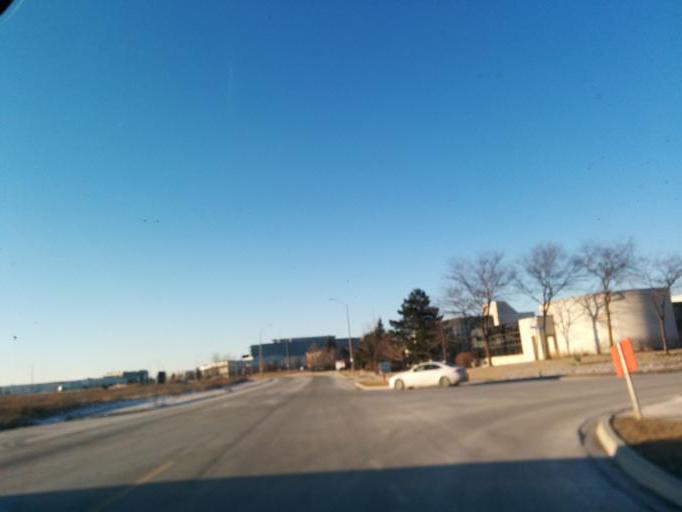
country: CA
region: Ontario
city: Etobicoke
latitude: 43.6529
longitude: -79.6050
